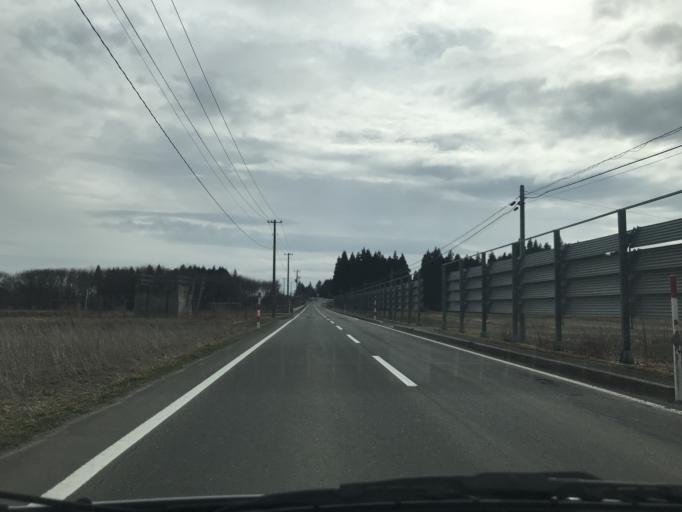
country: JP
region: Iwate
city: Hanamaki
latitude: 39.3803
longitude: 141.0078
